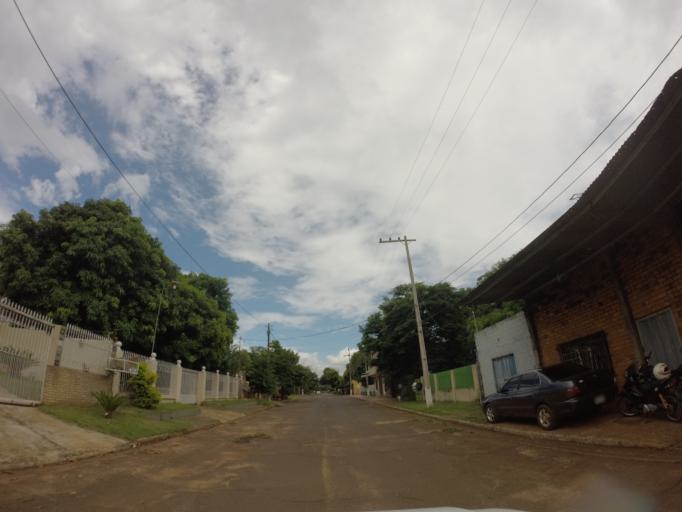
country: PY
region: Alto Parana
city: Ciudad del Este
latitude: -25.4165
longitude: -54.6291
